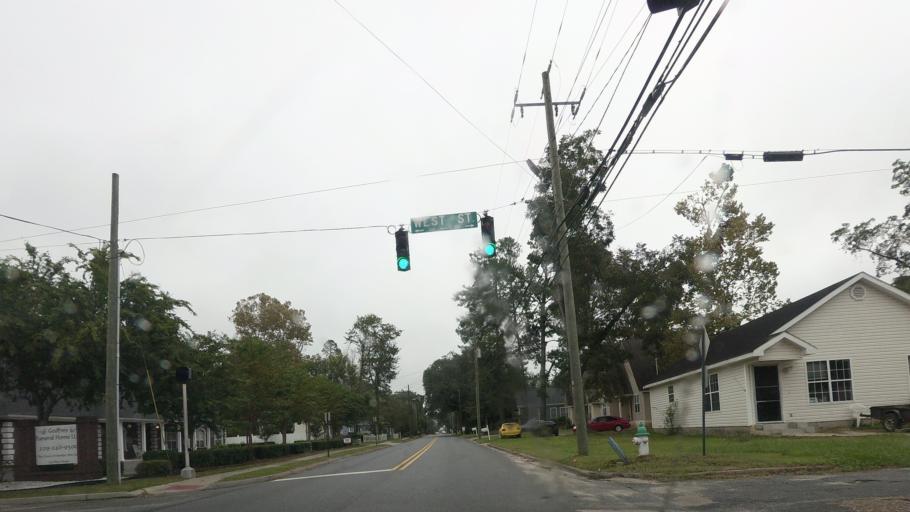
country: US
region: Georgia
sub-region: Lowndes County
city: Valdosta
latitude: 30.8304
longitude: -83.2909
